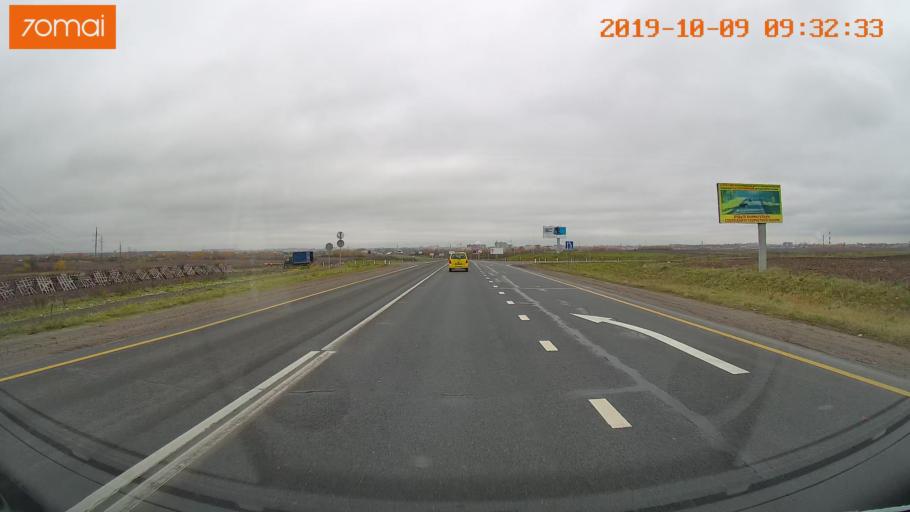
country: RU
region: Vologda
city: Vologda
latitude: 59.1596
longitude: 39.9273
